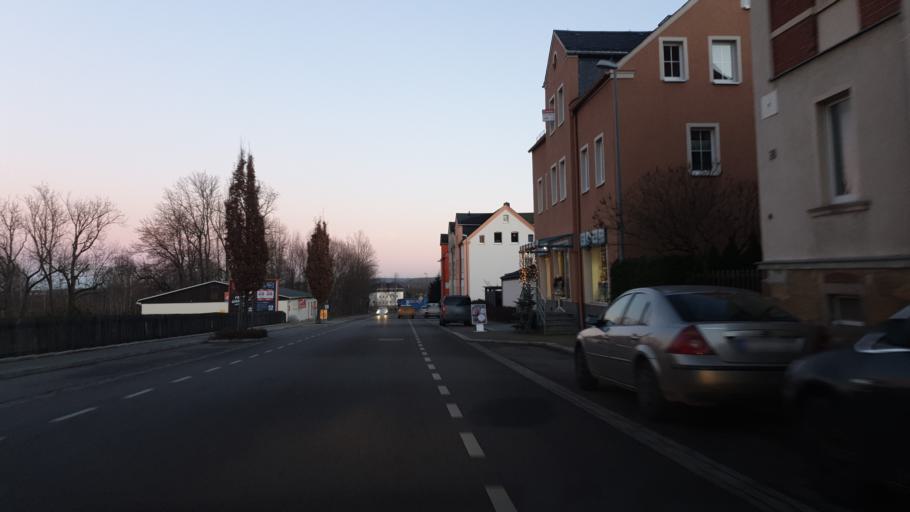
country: DE
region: Saxony
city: Hohndorf
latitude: 50.7364
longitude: 12.6882
